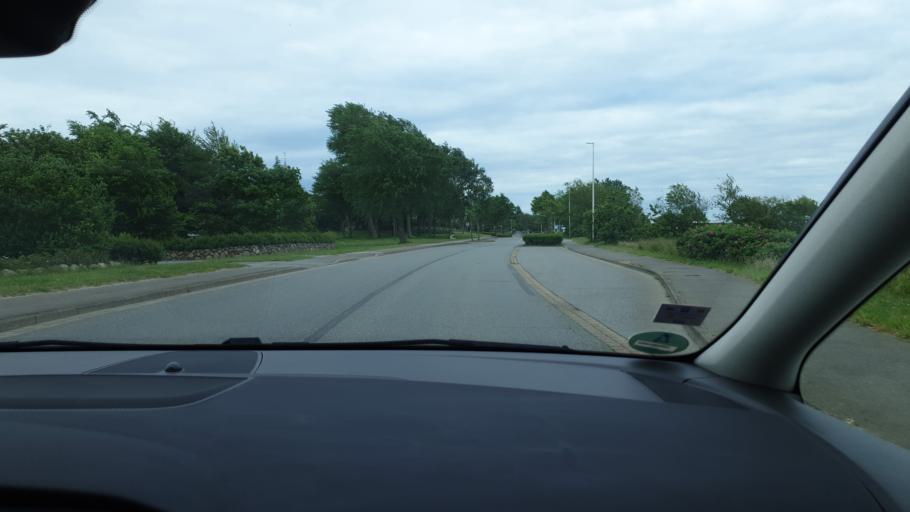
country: DE
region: Schleswig-Holstein
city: Schobull
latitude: 54.5111
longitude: 9.0022
